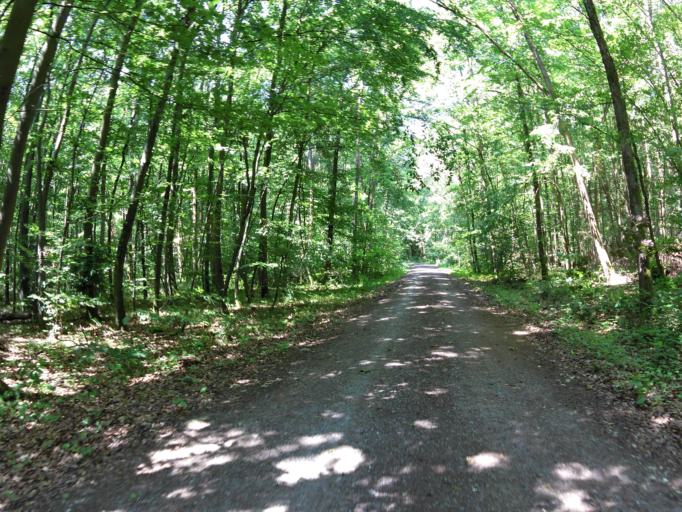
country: DE
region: Bavaria
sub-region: Regierungsbezirk Unterfranken
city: Kleinrinderfeld
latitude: 49.7169
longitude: 9.8541
